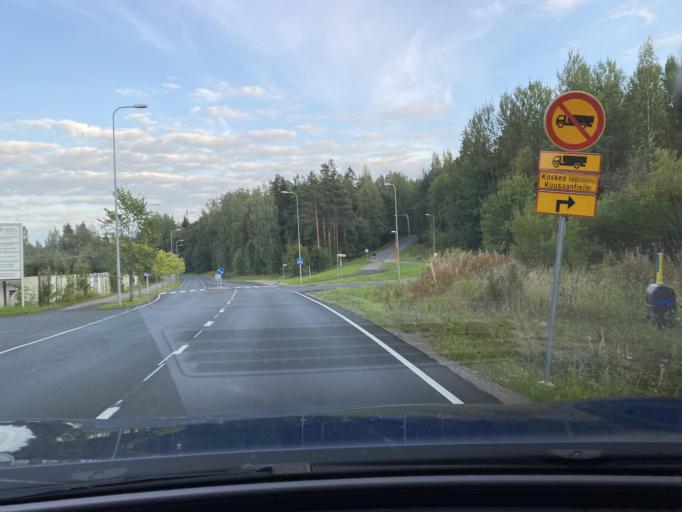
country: FI
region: Kymenlaakso
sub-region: Kouvola
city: Kouvola
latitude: 60.8999
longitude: 26.6502
